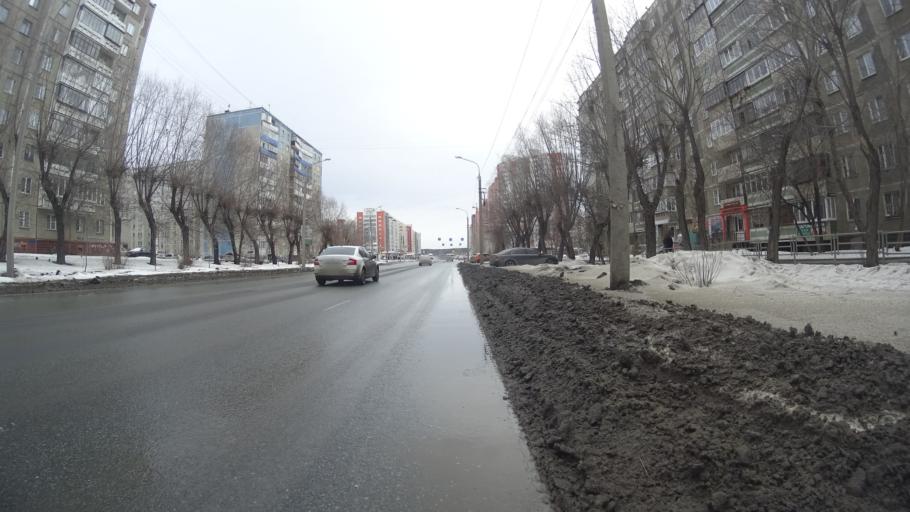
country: RU
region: Chelyabinsk
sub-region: Gorod Chelyabinsk
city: Chelyabinsk
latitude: 55.1779
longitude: 61.3099
